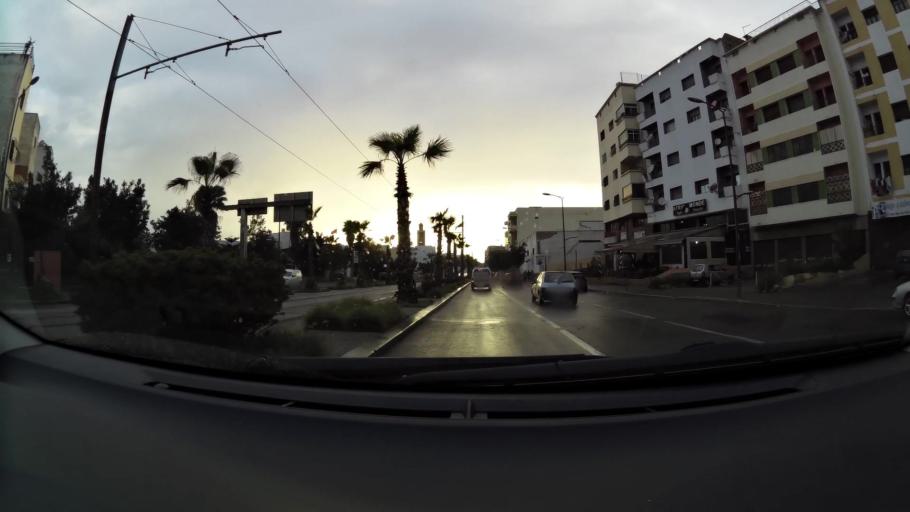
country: MA
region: Grand Casablanca
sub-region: Casablanca
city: Casablanca
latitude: 33.5794
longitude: -7.5583
